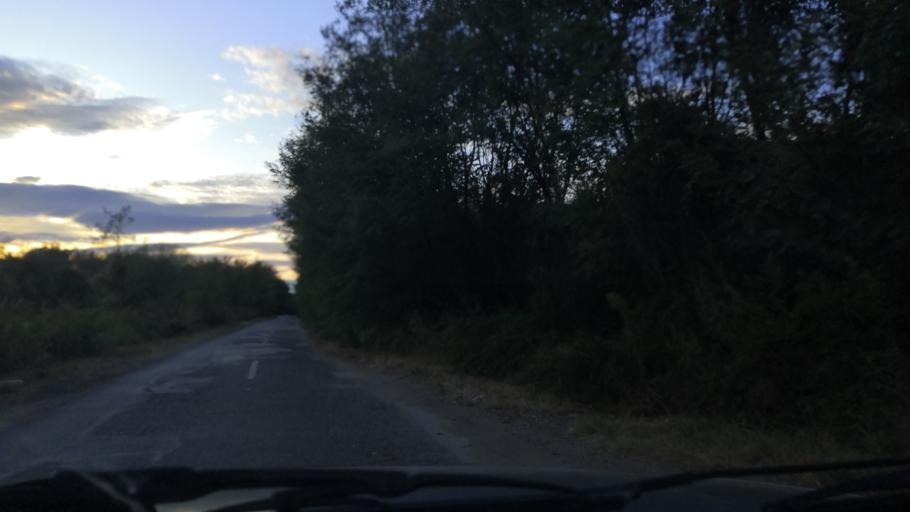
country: RO
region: Mehedinti
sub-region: Comuna Gruia
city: Izvoarele
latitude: 44.2817
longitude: 22.6423
